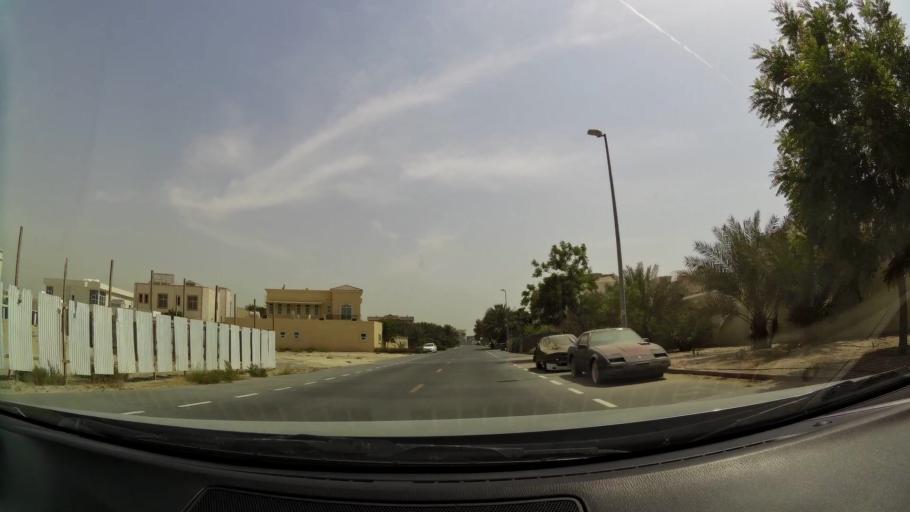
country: AE
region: Ash Shariqah
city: Sharjah
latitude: 25.2447
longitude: 55.4308
